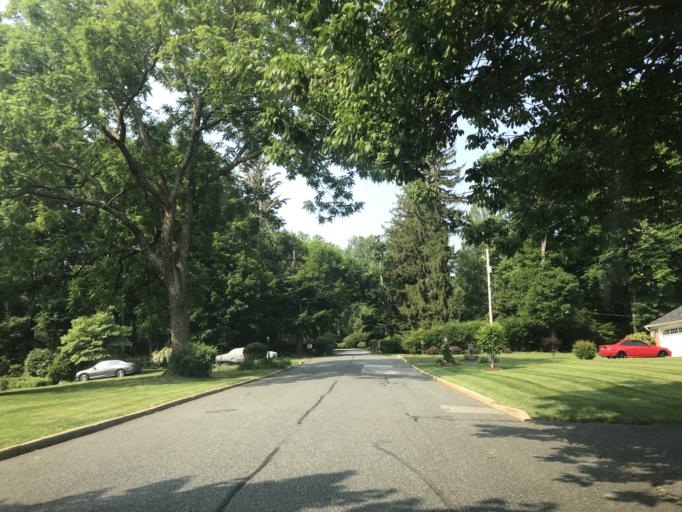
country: US
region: Maryland
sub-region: Harford County
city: North Bel Air
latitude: 39.5352
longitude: -76.3584
